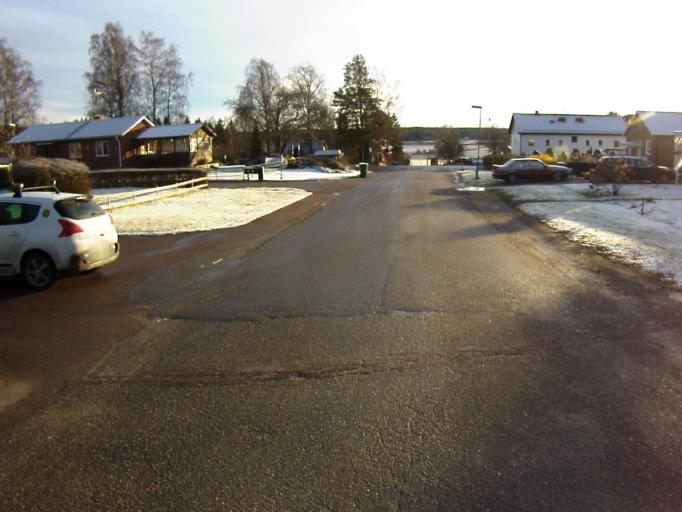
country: SE
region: Soedermanland
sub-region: Eskilstuna Kommun
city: Arla
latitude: 59.3186
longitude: 16.5925
